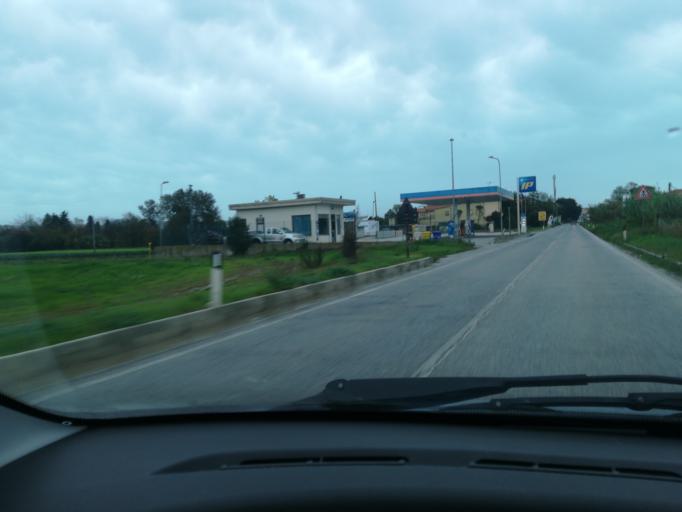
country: IT
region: The Marches
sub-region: Provincia di Macerata
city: Trodica
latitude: 43.2766
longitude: 13.6090
